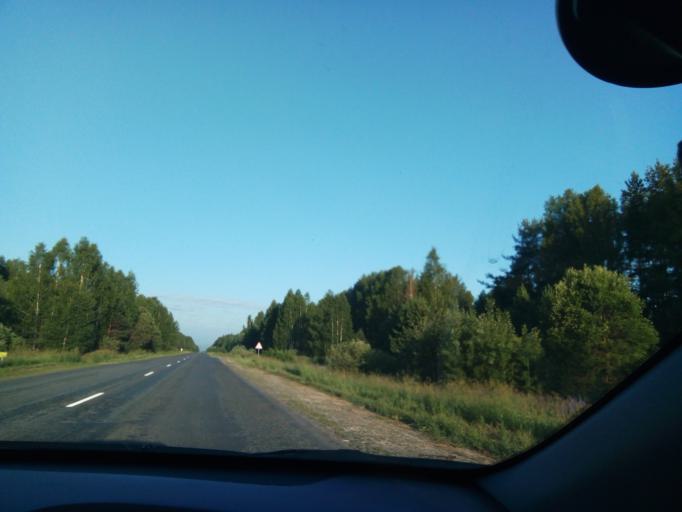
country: RU
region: Nizjnij Novgorod
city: Satis
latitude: 54.8968
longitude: 43.1156
